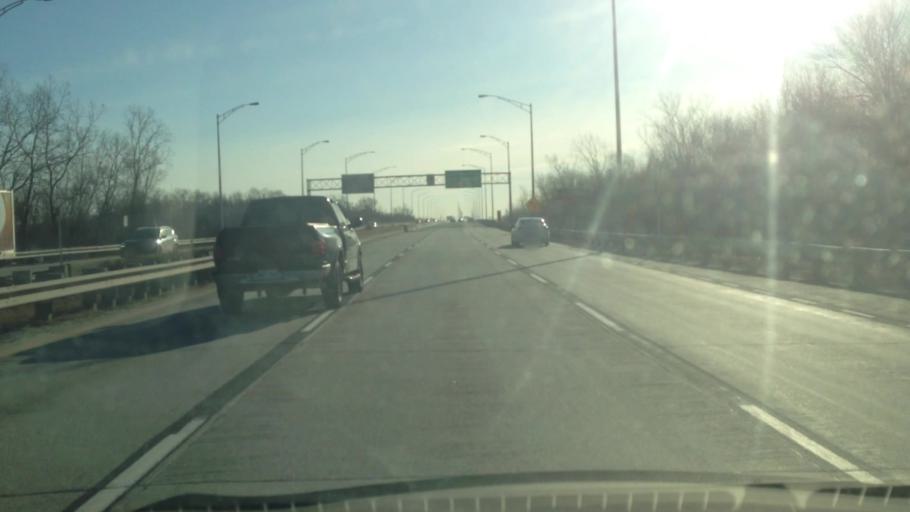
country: CA
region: Quebec
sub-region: Laurentides
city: Boisbriand
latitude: 45.5846
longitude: -73.8418
